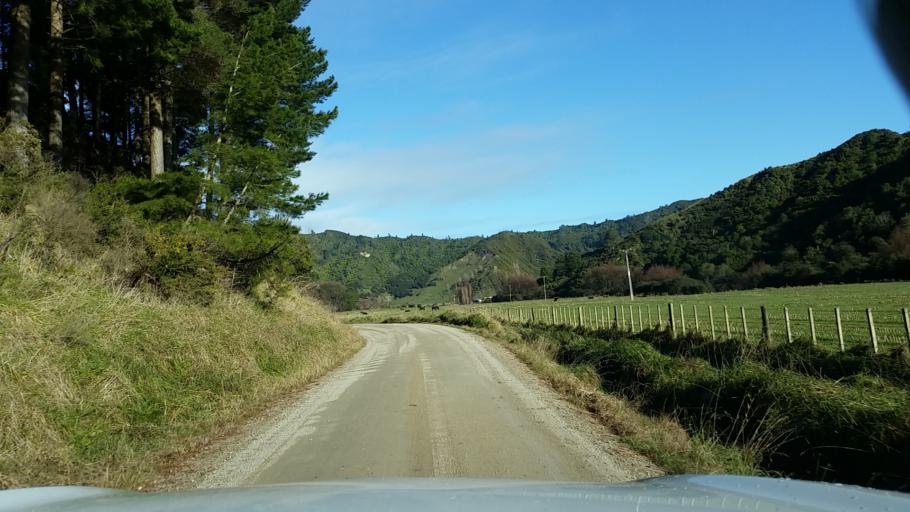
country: NZ
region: Taranaki
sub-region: South Taranaki District
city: Patea
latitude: -39.7002
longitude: 174.7313
